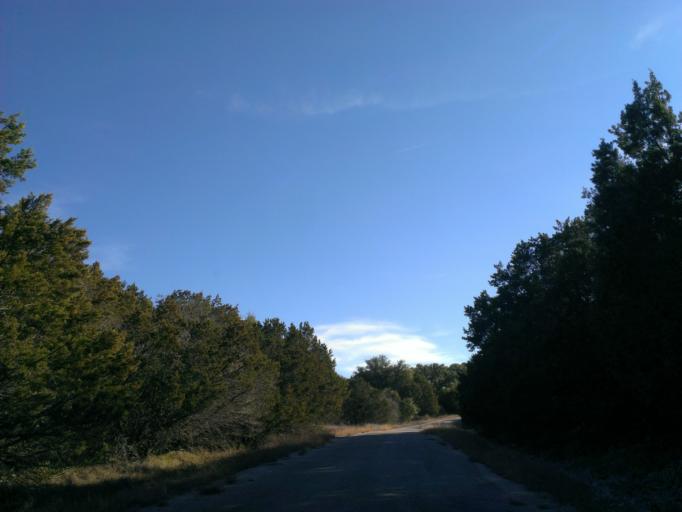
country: US
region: Texas
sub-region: Llano County
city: Horseshoe Bay
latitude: 30.5367
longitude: -98.3362
